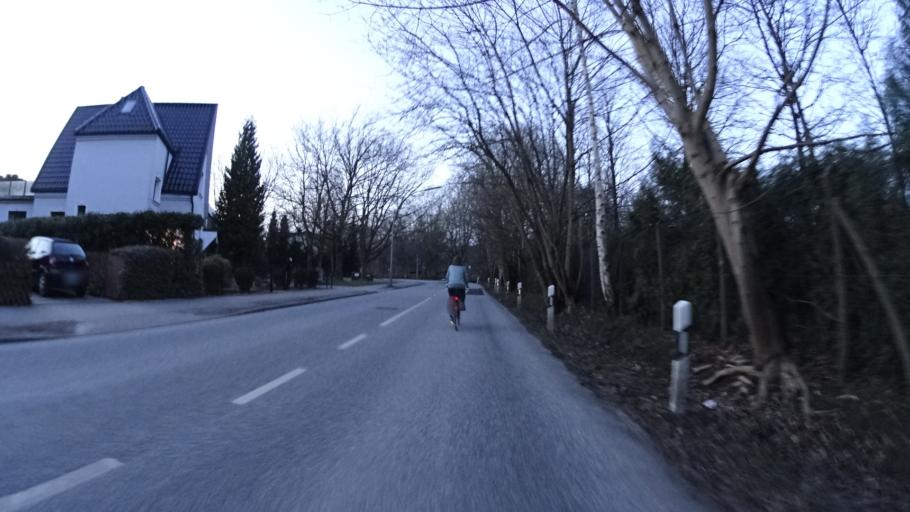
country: DE
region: Hamburg
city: Stellingen
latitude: 53.6002
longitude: 9.9313
